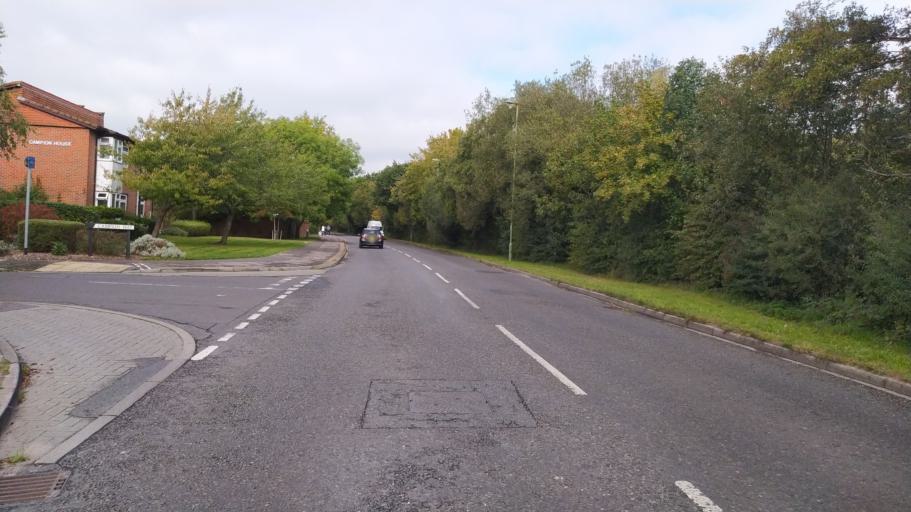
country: GB
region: England
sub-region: Hampshire
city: Lymington
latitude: 50.7664
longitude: -1.5441
